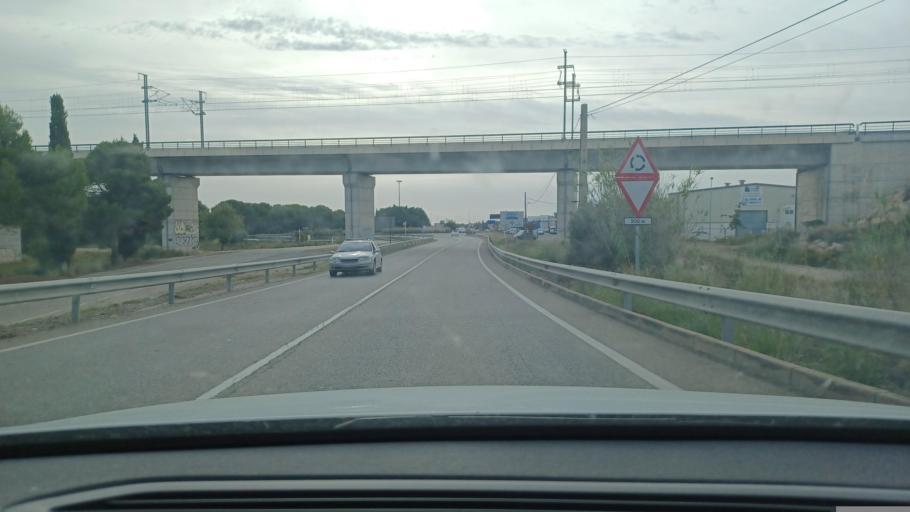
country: ES
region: Catalonia
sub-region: Provincia de Tarragona
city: Cambrils
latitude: 41.0799
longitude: 1.0389
